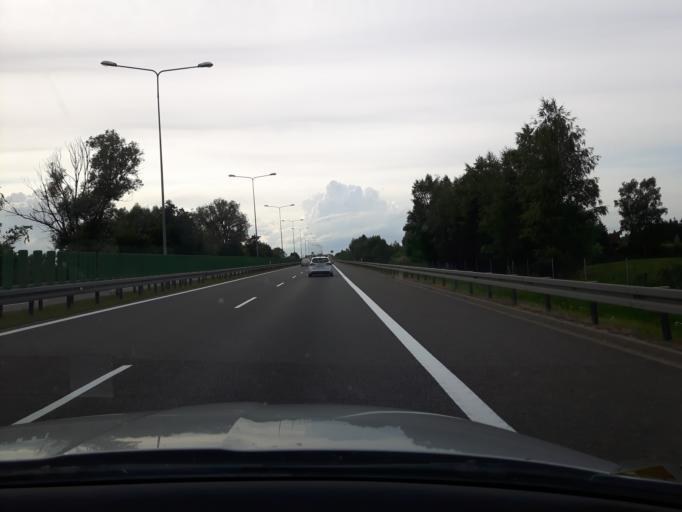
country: PL
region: Warmian-Masurian Voivodeship
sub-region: Powiat elblaski
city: Elblag
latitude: 54.1405
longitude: 19.4044
